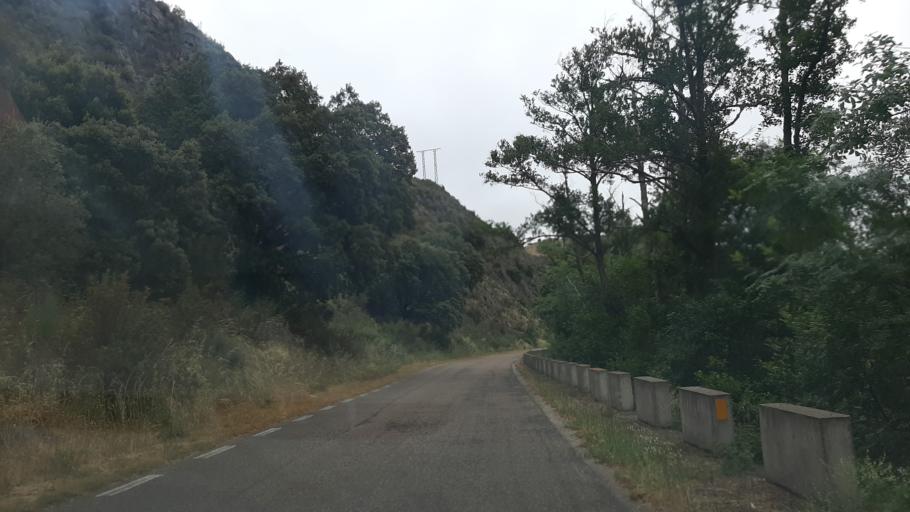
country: ES
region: Castille and Leon
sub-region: Provincia de Salamanca
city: Pastores
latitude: 40.5413
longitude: -6.4865
